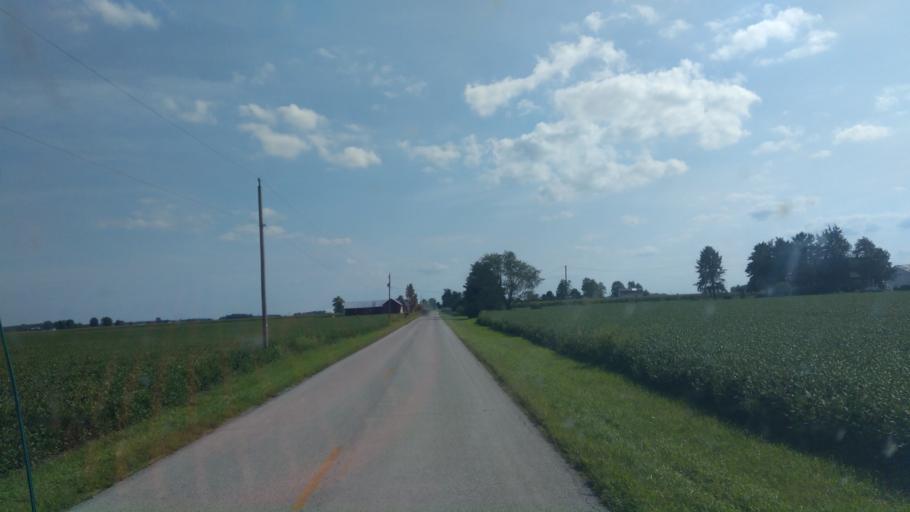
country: US
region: Ohio
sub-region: Hardin County
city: Kenton
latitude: 40.6929
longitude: -83.5144
